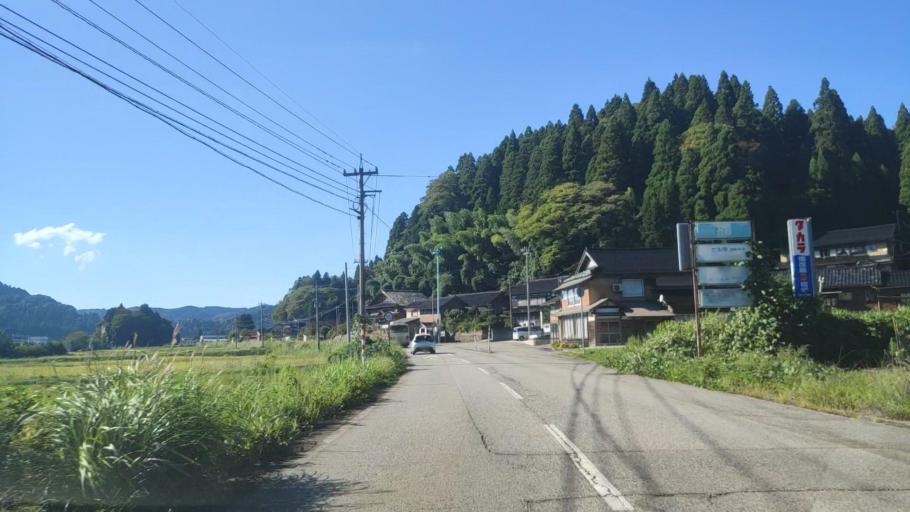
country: JP
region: Ishikawa
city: Nanao
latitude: 37.2777
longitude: 137.0521
